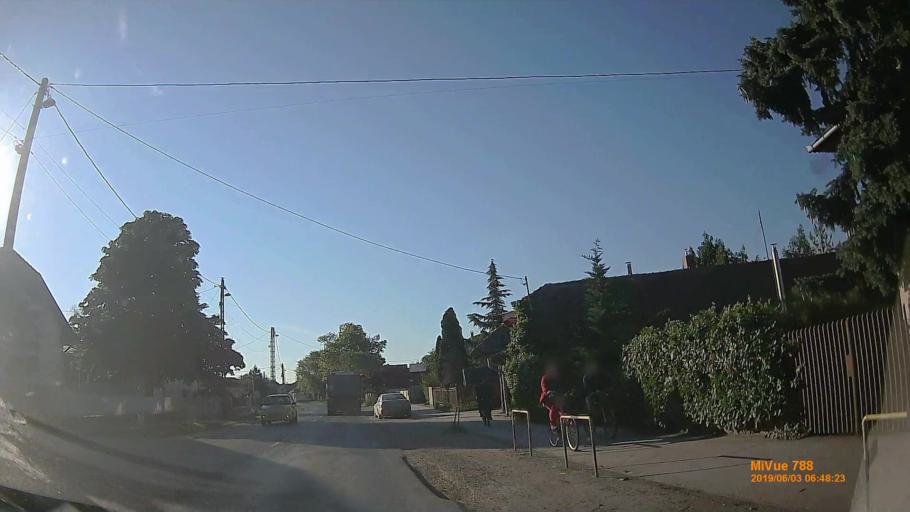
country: HU
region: Pest
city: Bugyi
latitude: 47.2233
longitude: 19.1538
